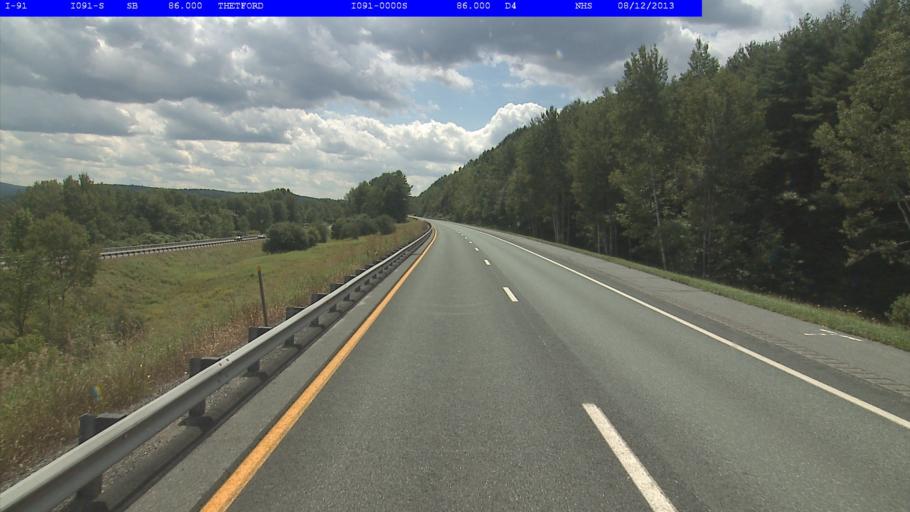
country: US
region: New Hampshire
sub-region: Grafton County
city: Lyme
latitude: 43.8369
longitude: -72.2045
